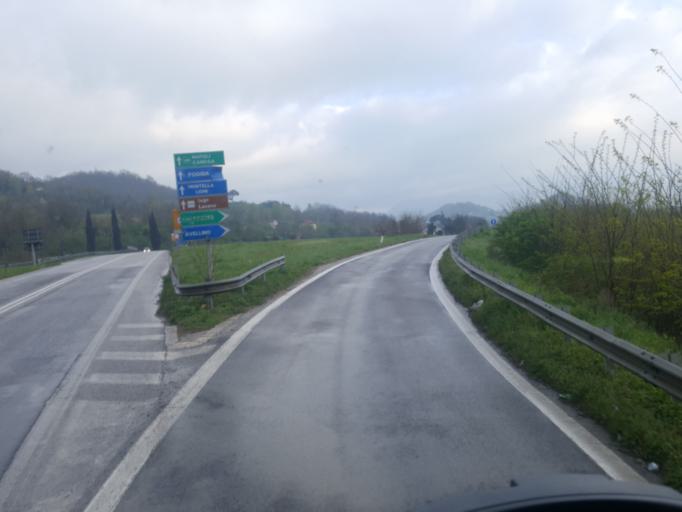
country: IT
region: Campania
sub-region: Provincia di Avellino
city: Manocalzati
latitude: 40.9374
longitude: 14.8301
